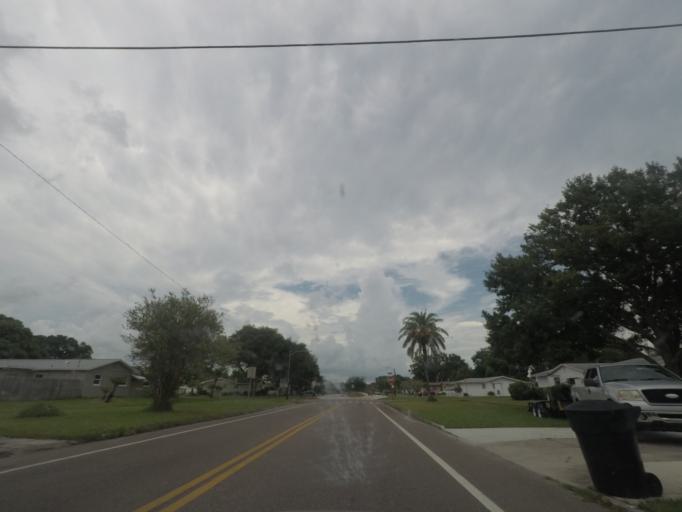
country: US
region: Florida
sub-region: Pinellas County
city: Kenneth City
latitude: 27.7990
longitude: -82.7176
